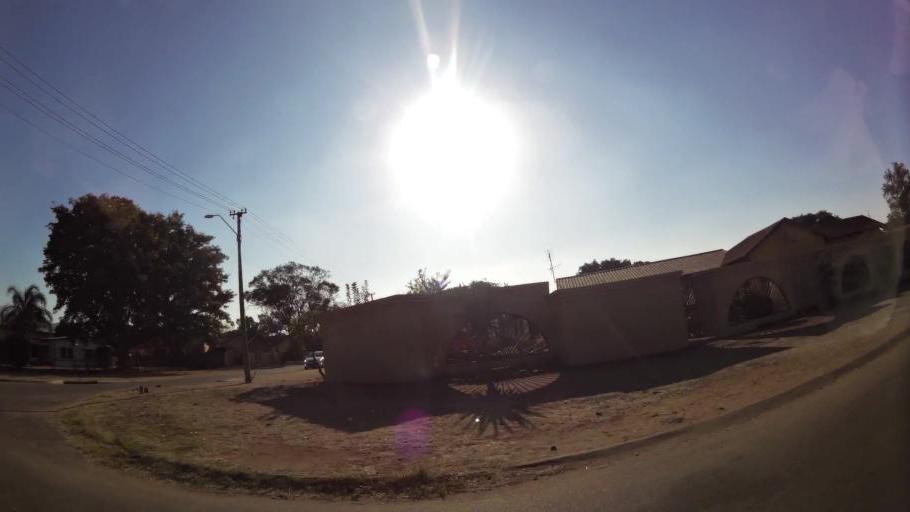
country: ZA
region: North-West
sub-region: Bojanala Platinum District Municipality
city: Rustenburg
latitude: -25.6491
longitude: 27.2291
